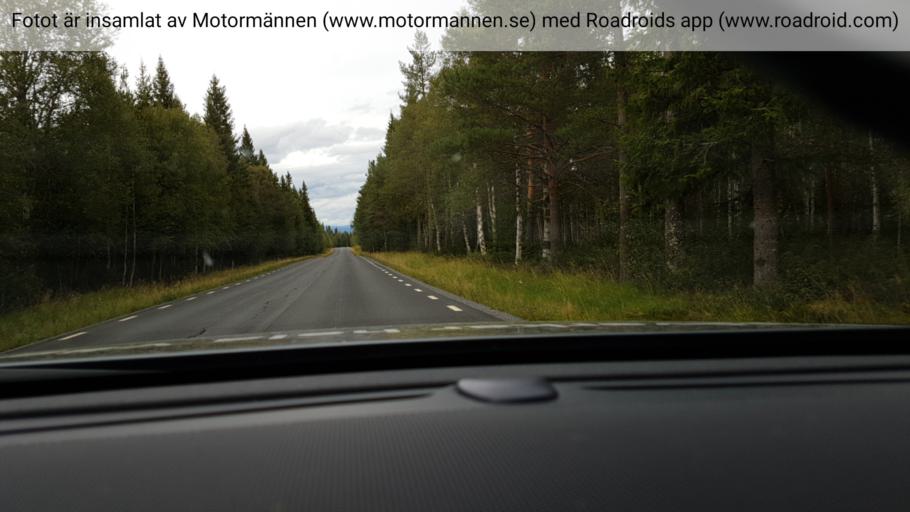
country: NO
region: Hedmark
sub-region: Trysil
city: Innbygda
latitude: 61.6614
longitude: 12.9922
